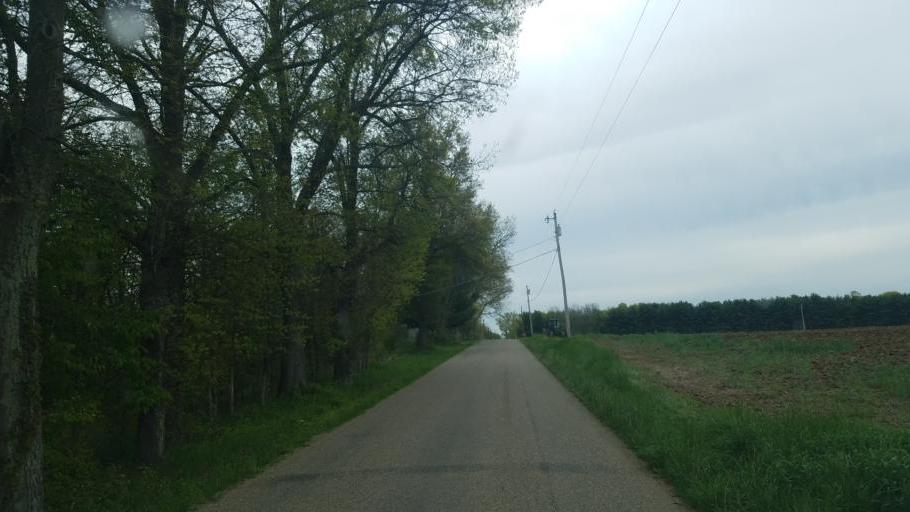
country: US
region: Ohio
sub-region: Knox County
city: Gambier
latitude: 40.3864
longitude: -82.3705
